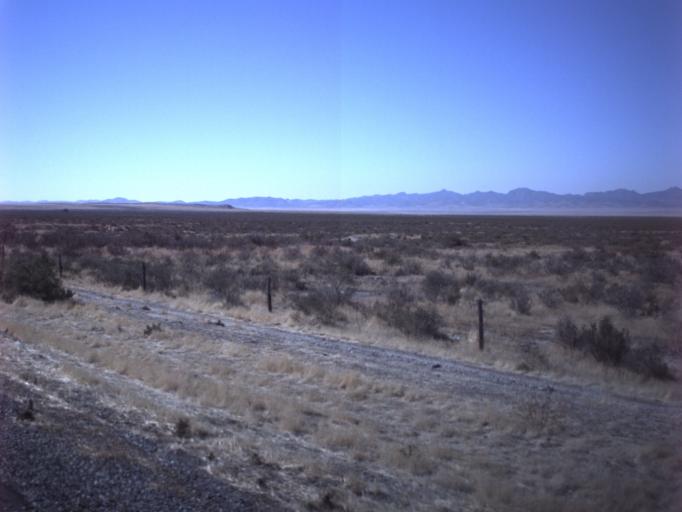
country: US
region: Utah
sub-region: Tooele County
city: Grantsville
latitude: 40.4756
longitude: -112.7460
